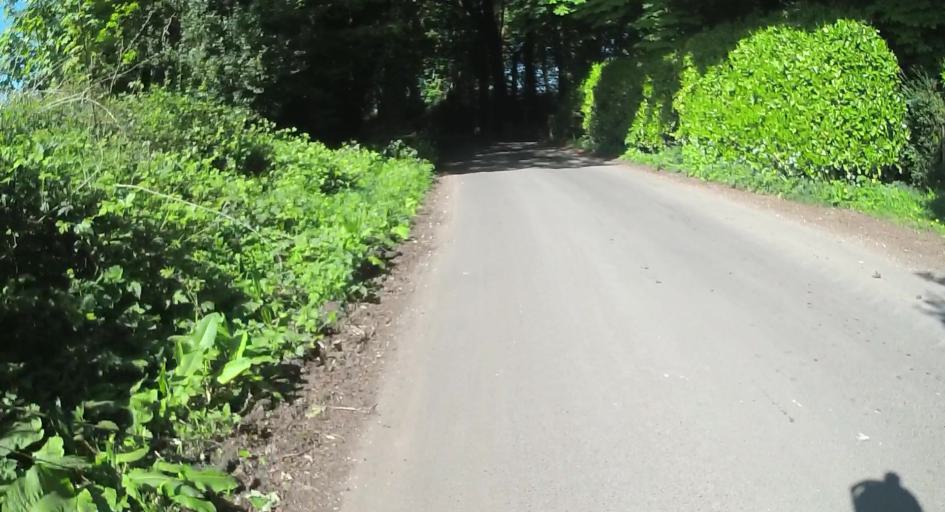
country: GB
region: England
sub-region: Hampshire
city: Alton
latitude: 51.1797
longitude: -1.0031
